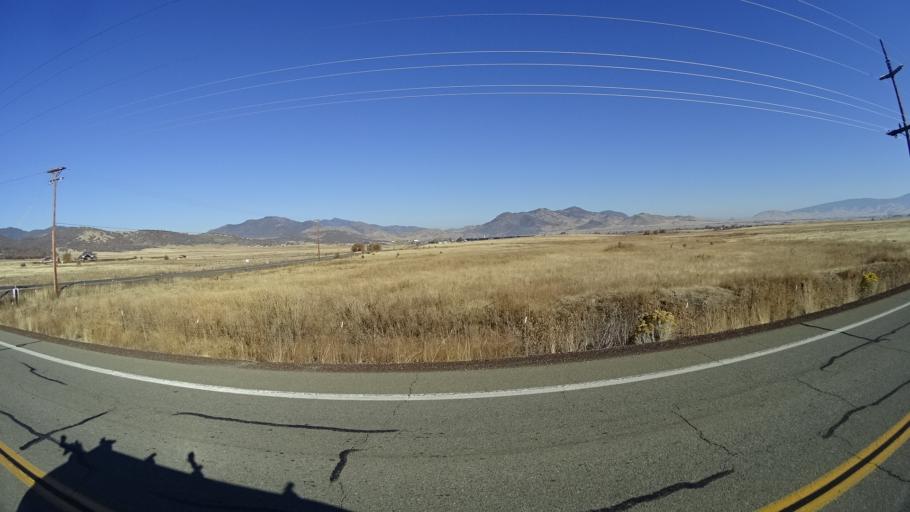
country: US
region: California
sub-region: Siskiyou County
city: Yreka
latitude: 41.7112
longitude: -122.5930
